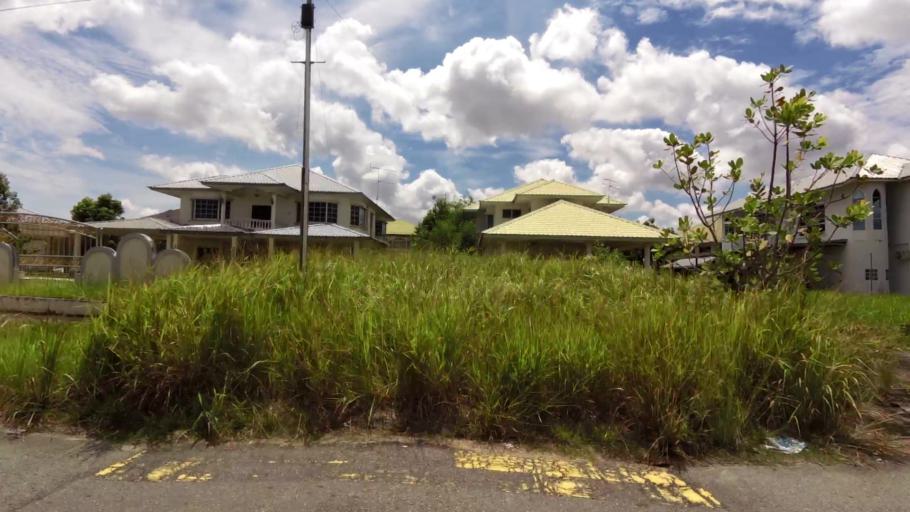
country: BN
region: Brunei and Muara
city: Bandar Seri Begawan
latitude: 4.9494
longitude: 114.9121
